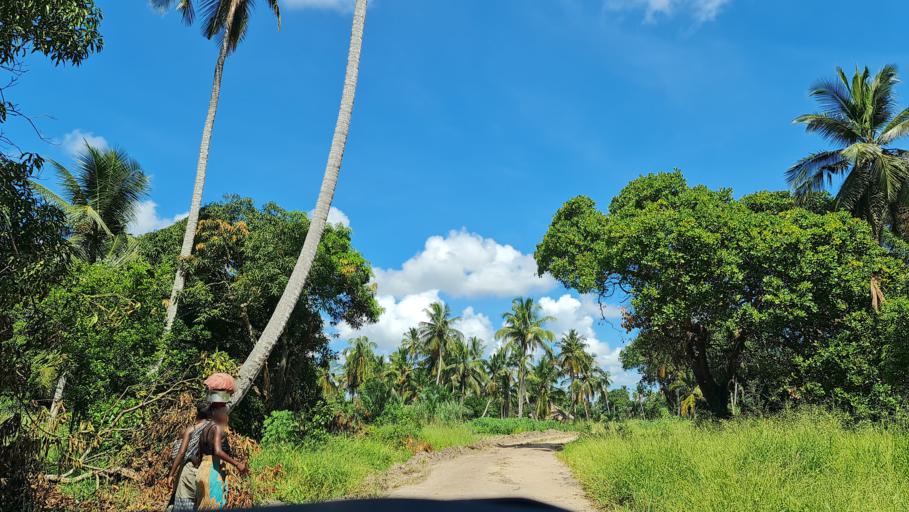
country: MZ
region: Zambezia
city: Quelimane
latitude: -17.3833
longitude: 37.5210
